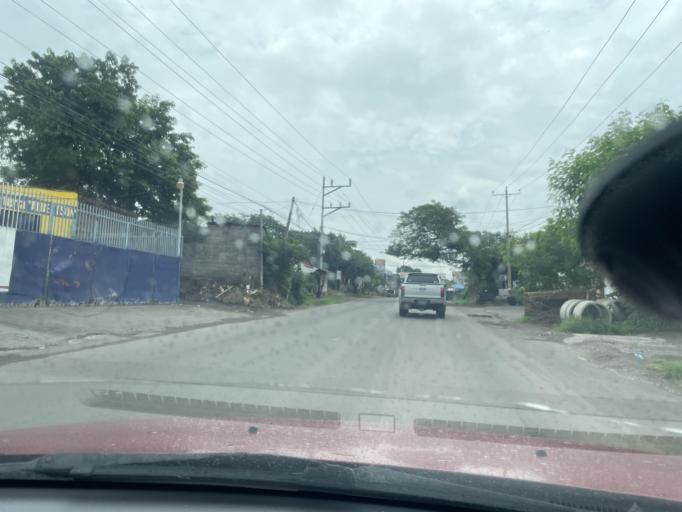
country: SV
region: La Union
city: Santa Rosa de Lima
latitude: 13.6295
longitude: -87.8925
